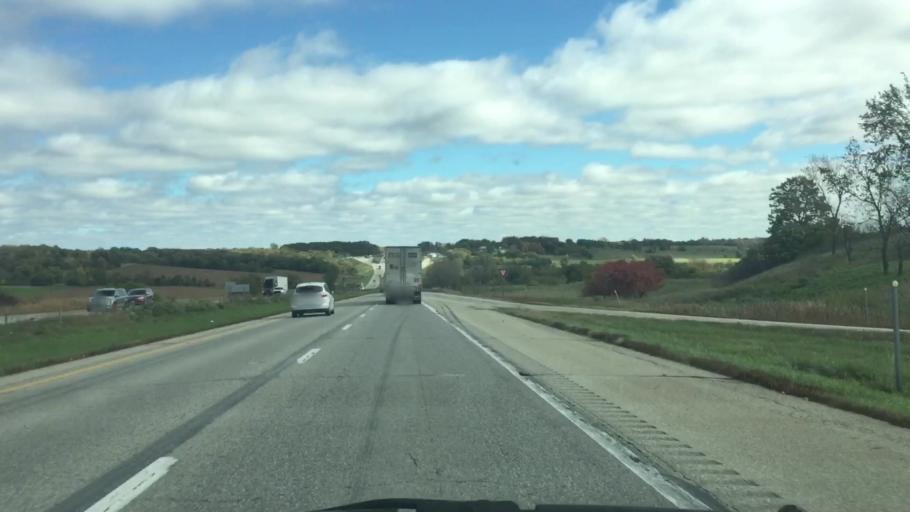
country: US
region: Iowa
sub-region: Poweshiek County
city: Grinnell
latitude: 41.6951
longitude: -92.7908
